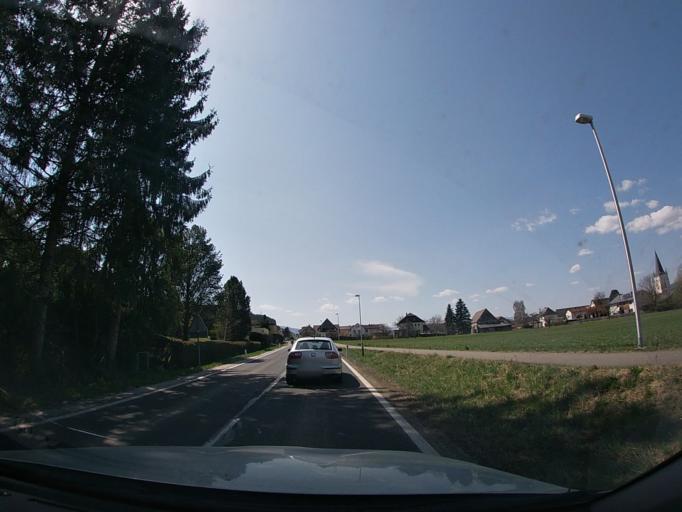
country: AT
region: Styria
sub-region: Politischer Bezirk Murtal
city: Sankt Margarethen bei Knittelfeld
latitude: 47.2288
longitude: 14.8606
